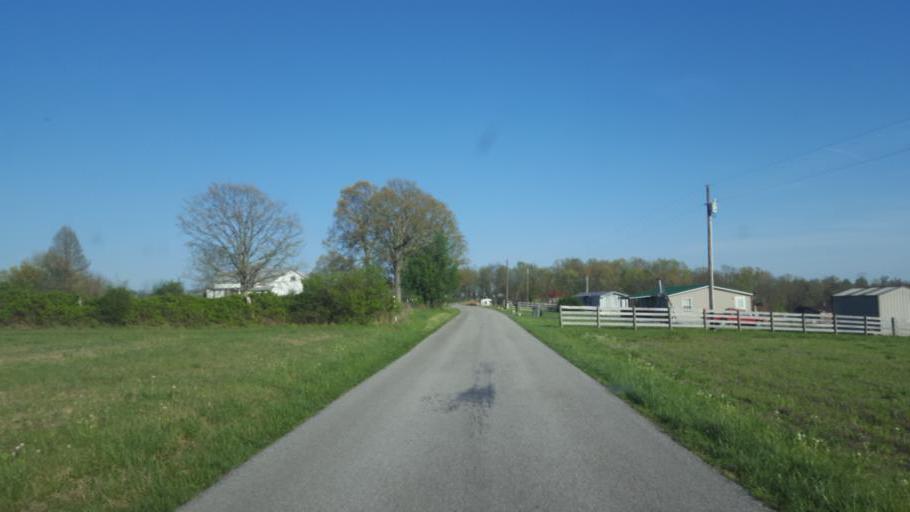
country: US
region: Kentucky
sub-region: Barren County
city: Cave City
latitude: 37.1740
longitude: -85.9954
